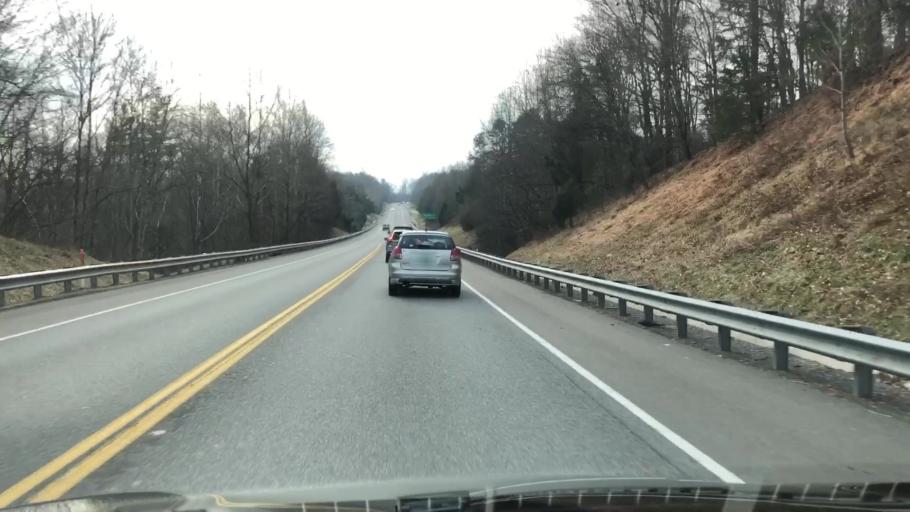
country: US
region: Virginia
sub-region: City of Lynchburg
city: West Lynchburg
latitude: 37.4293
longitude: -79.2352
